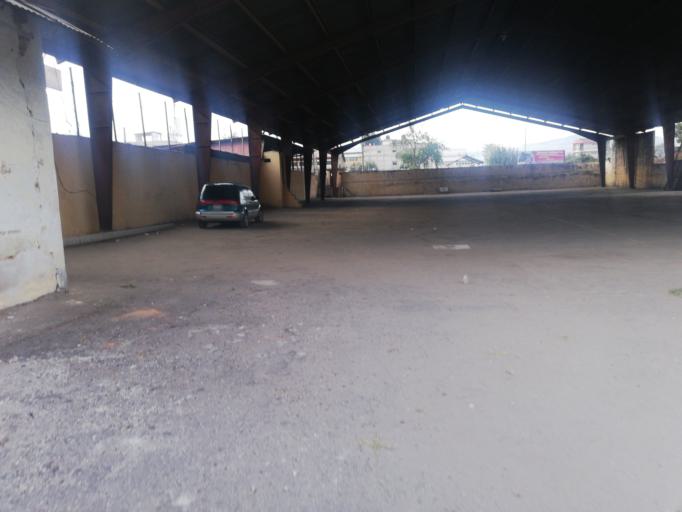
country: GT
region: Quetzaltenango
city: Quetzaltenango
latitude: 14.8469
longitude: -91.5242
